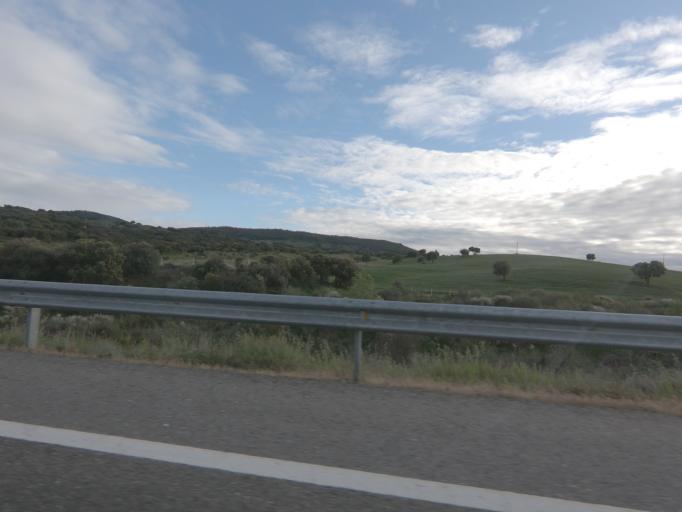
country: ES
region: Extremadura
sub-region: Provincia de Caceres
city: Pedroso de Acim
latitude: 39.8340
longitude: -6.3899
